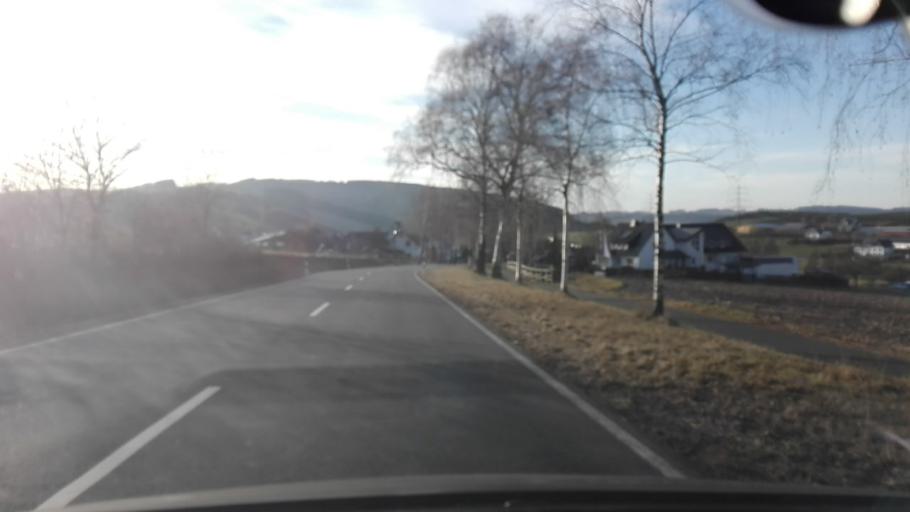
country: DE
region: North Rhine-Westphalia
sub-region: Regierungsbezirk Arnsberg
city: Schmallenberg
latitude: 51.1554
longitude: 8.2561
